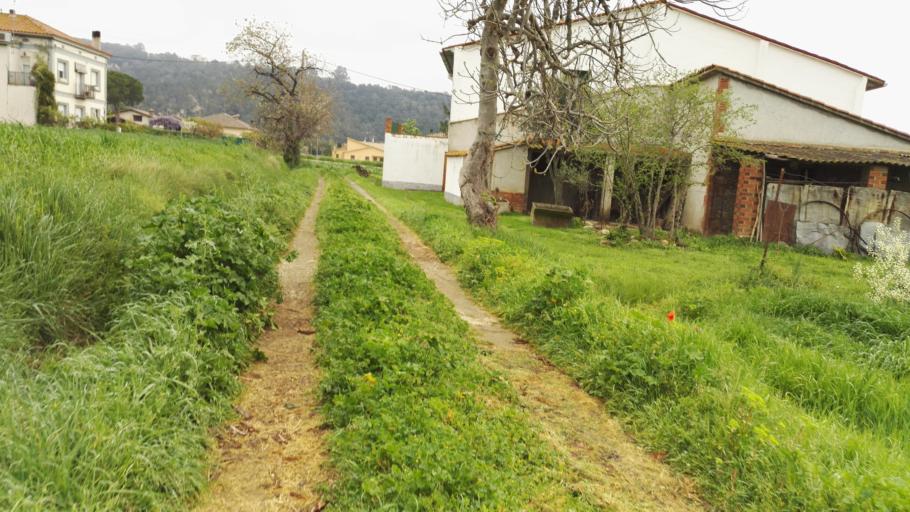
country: ES
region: Catalonia
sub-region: Provincia de Barcelona
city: Santa Maria de Palautordera
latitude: 41.7144
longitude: 2.4263
